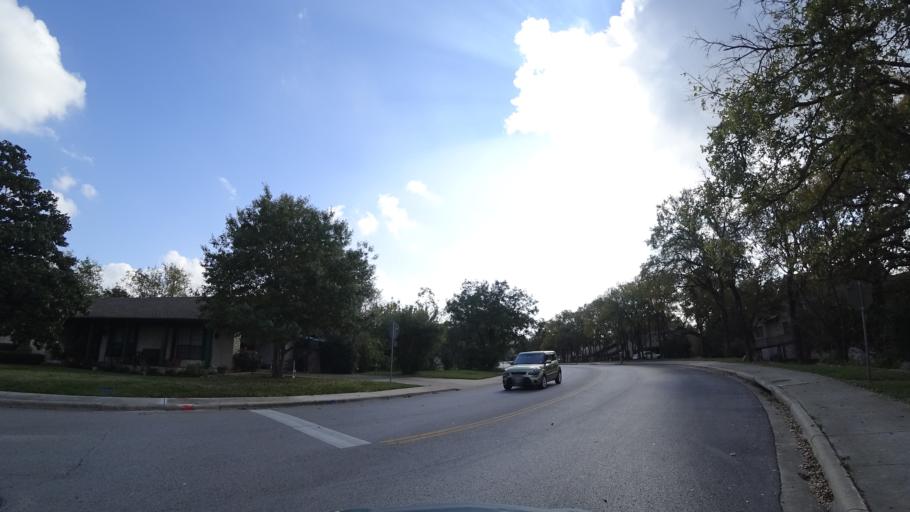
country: US
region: Texas
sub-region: Williamson County
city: Round Rock
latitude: 30.5047
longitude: -97.6744
